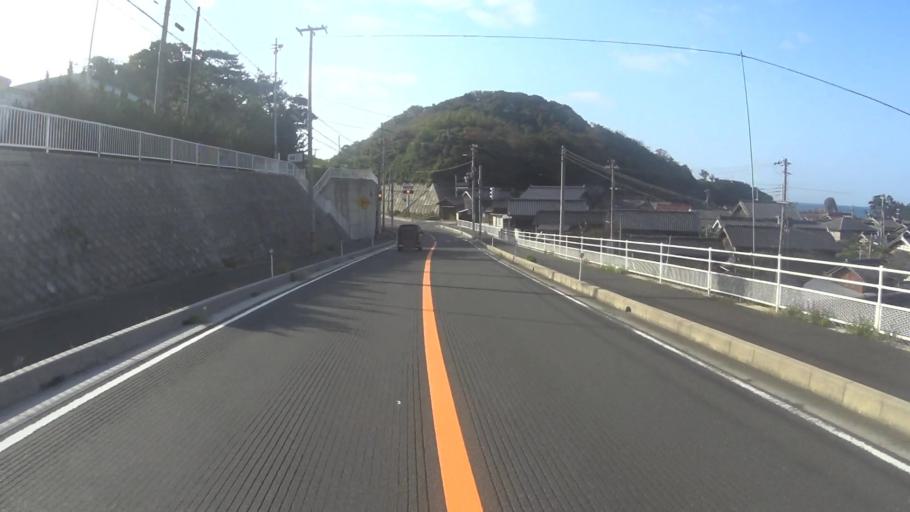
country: JP
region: Kyoto
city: Miyazu
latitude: 35.7414
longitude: 135.1131
